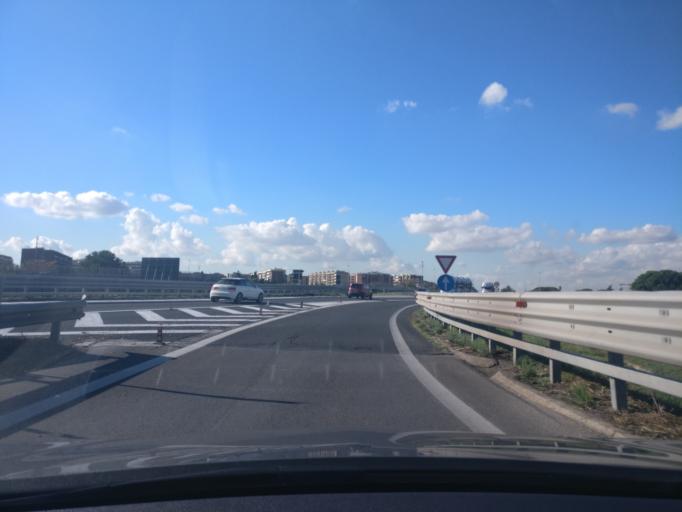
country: IT
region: Latium
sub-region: Citta metropolitana di Roma Capitale
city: Ciampino
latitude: 41.8525
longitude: 12.5997
